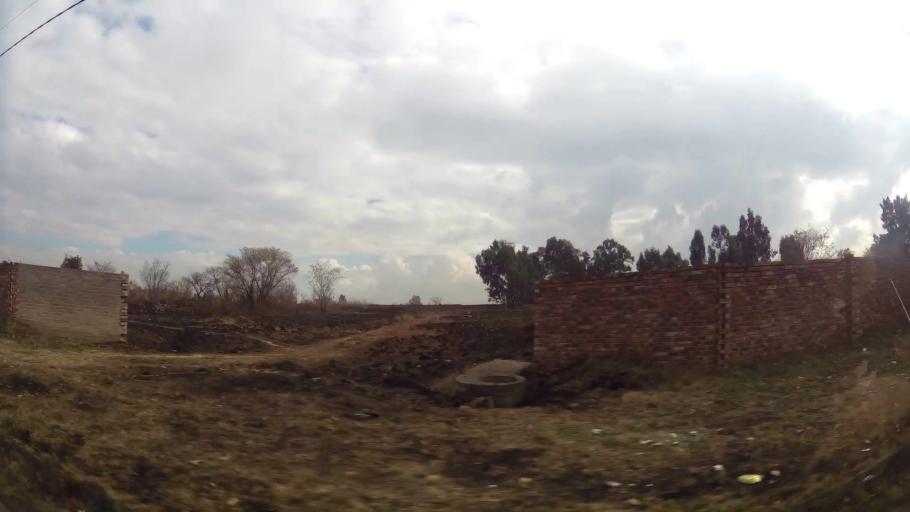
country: ZA
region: Gauteng
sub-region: Sedibeng District Municipality
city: Meyerton
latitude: -26.6004
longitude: 27.9994
